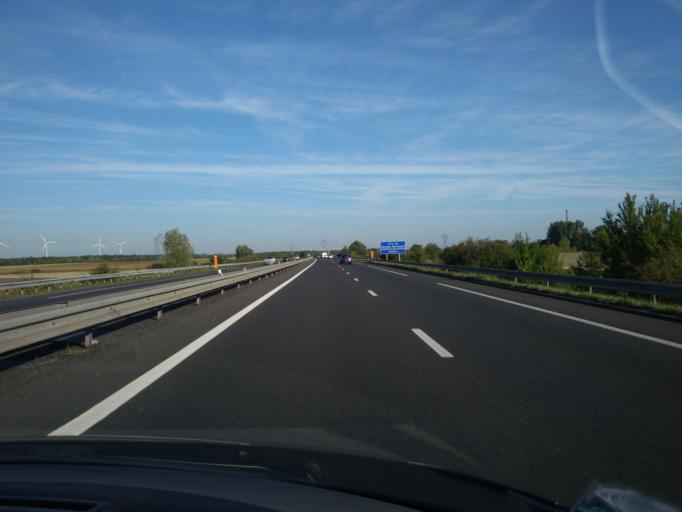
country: FR
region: Centre
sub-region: Departement du Cher
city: Marmagne
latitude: 47.0812
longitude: 2.2677
